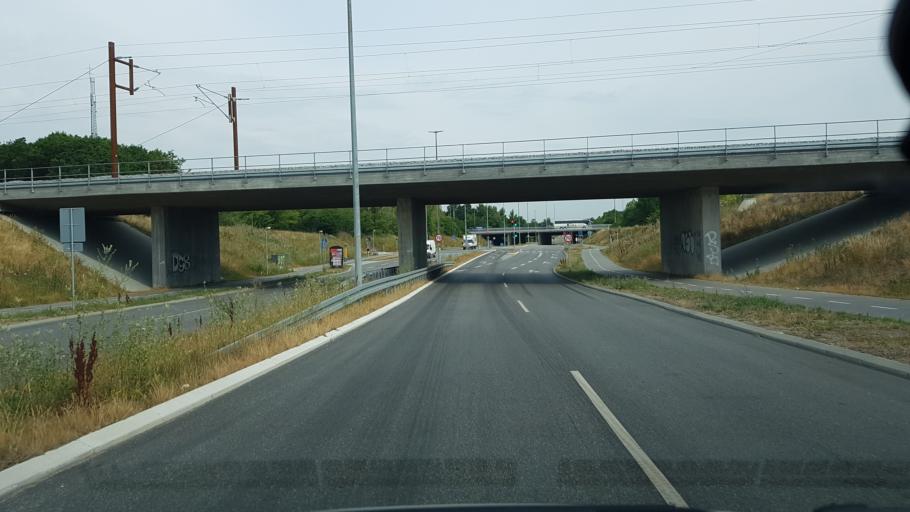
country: DK
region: Capital Region
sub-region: Brondby Kommune
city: Brondbyvester
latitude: 55.6389
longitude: 12.4181
